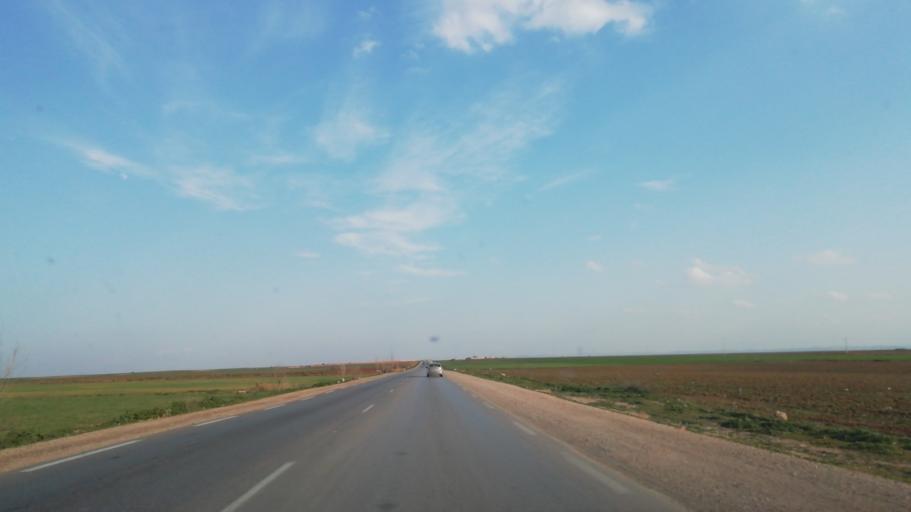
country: DZ
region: Relizane
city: Relizane
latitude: 35.8960
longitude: 0.5984
